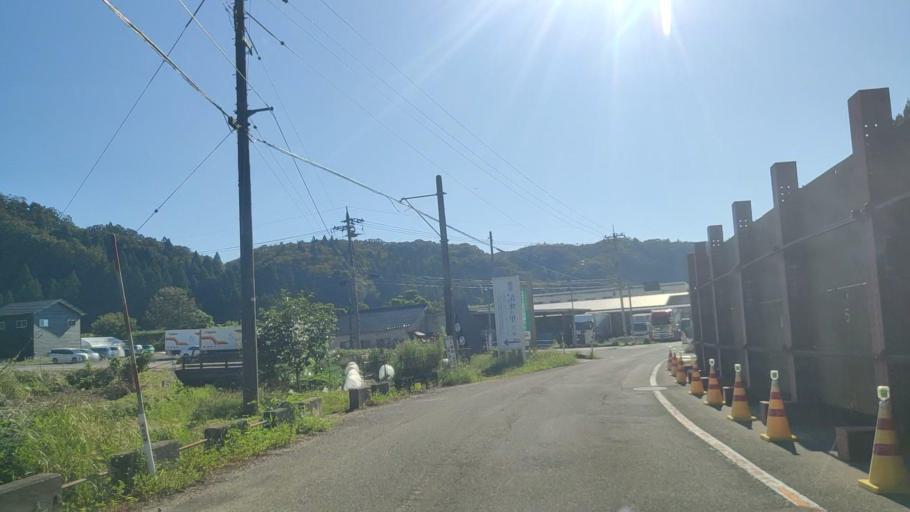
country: JP
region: Ishikawa
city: Nanao
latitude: 37.2349
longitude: 136.9746
